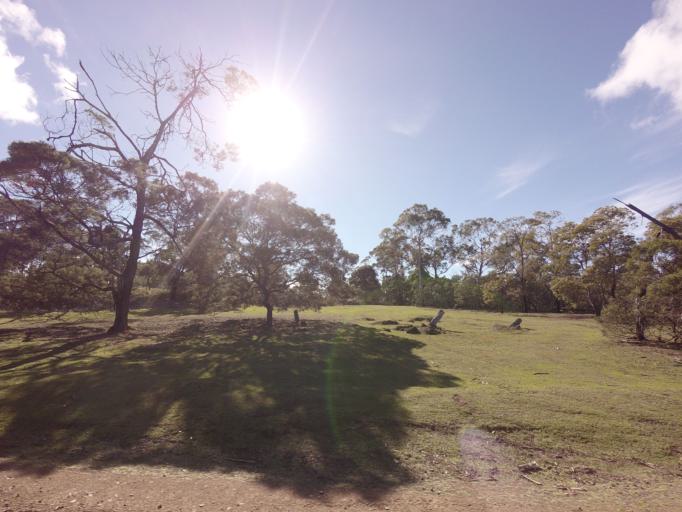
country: AU
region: Tasmania
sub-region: Clarence
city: Sandford
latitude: -42.9639
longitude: 147.7053
